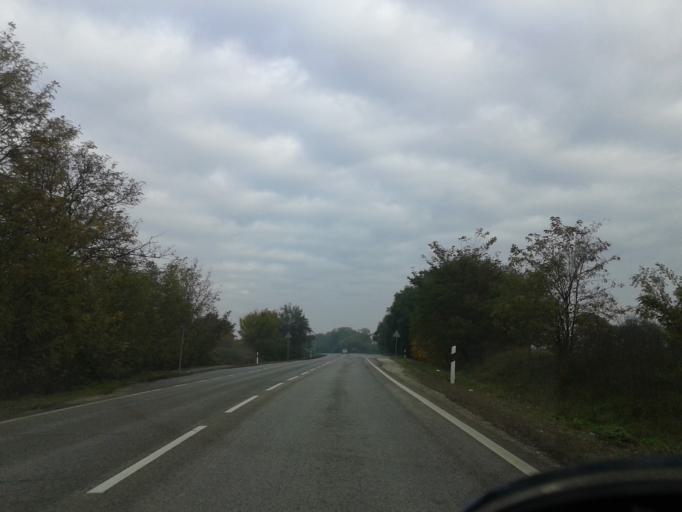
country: HU
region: Pest
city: Szazhalombatta
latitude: 47.3019
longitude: 18.8850
